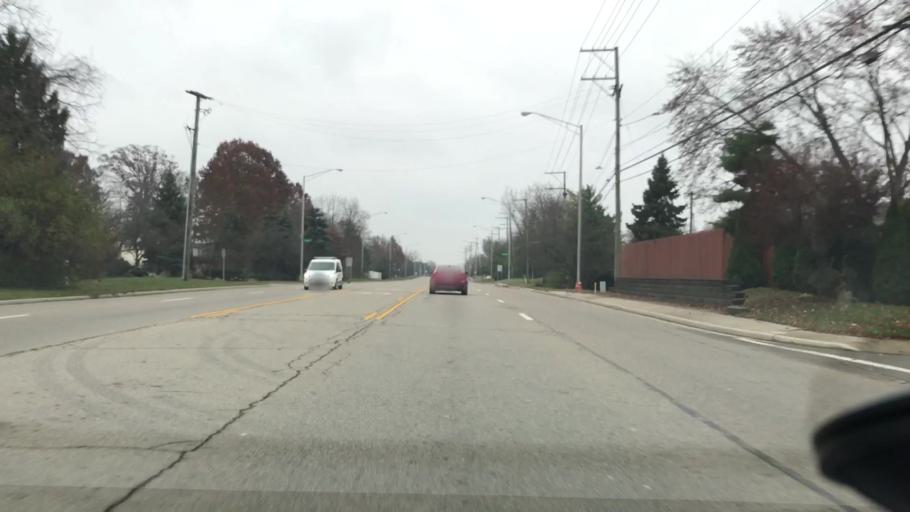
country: US
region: Ohio
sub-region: Franklin County
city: Lincoln Village
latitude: 39.9843
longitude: -83.1056
